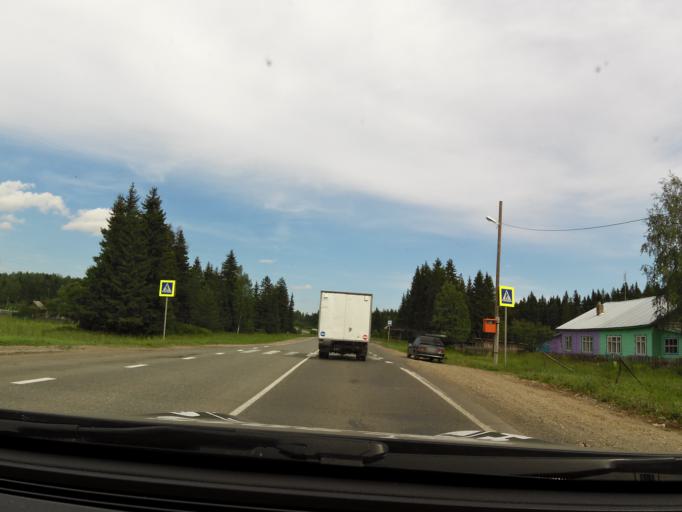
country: RU
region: Kirov
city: Vakhrushi
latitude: 58.6923
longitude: 50.0568
